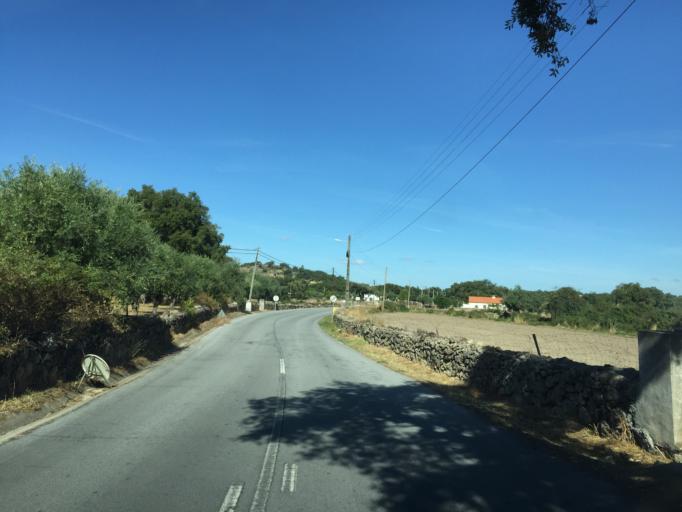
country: PT
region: Portalegre
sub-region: Marvao
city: Marvao
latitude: 39.4261
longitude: -7.3544
